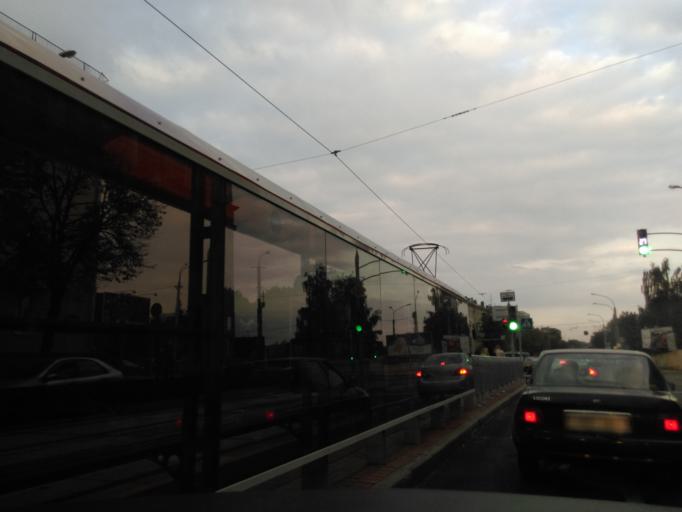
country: BY
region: Minsk
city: Minsk
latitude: 53.9063
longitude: 27.5903
